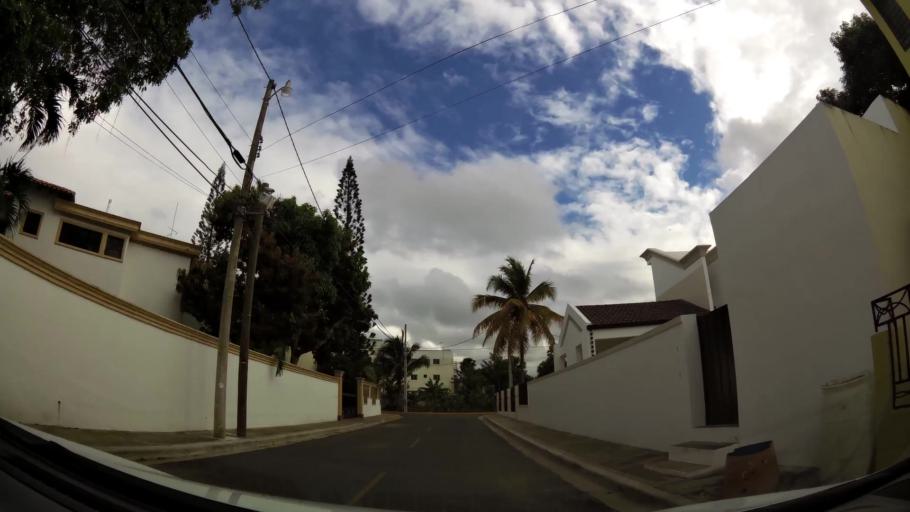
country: DO
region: Santiago
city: Santiago de los Caballeros
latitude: 19.4654
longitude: -70.6540
